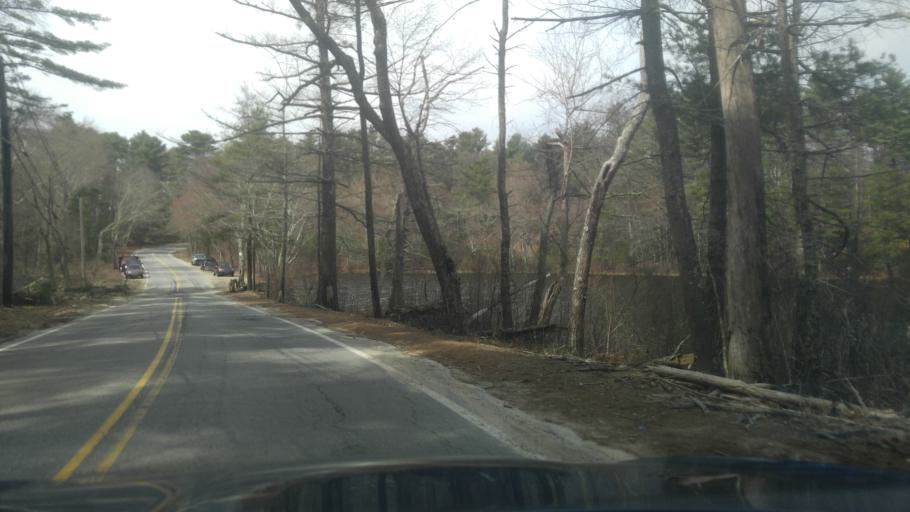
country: US
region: Rhode Island
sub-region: Washington County
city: Exeter
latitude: 41.6359
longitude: -71.5730
